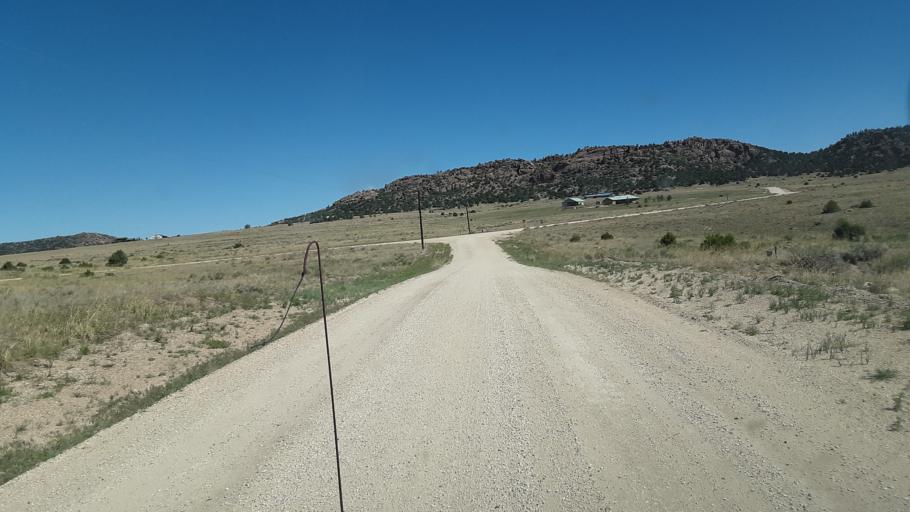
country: US
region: Colorado
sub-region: Custer County
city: Westcliffe
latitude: 38.2246
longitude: -105.4584
